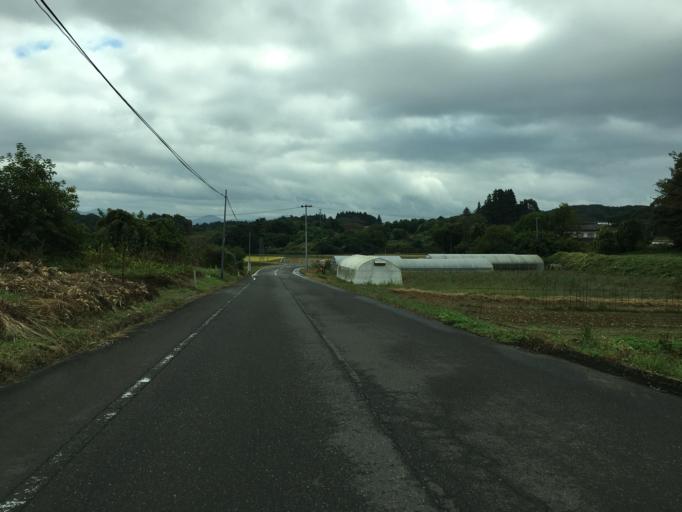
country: JP
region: Fukushima
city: Nihommatsu
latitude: 37.6284
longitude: 140.4434
